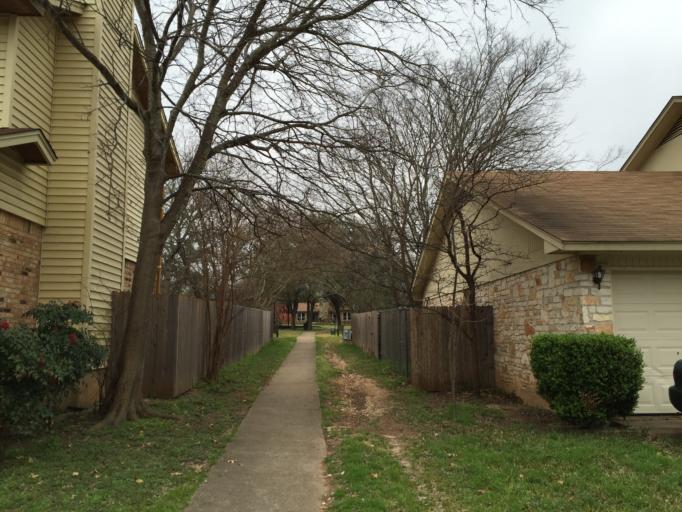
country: US
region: Texas
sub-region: Williamson County
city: Anderson Mill
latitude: 30.4504
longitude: -97.8100
